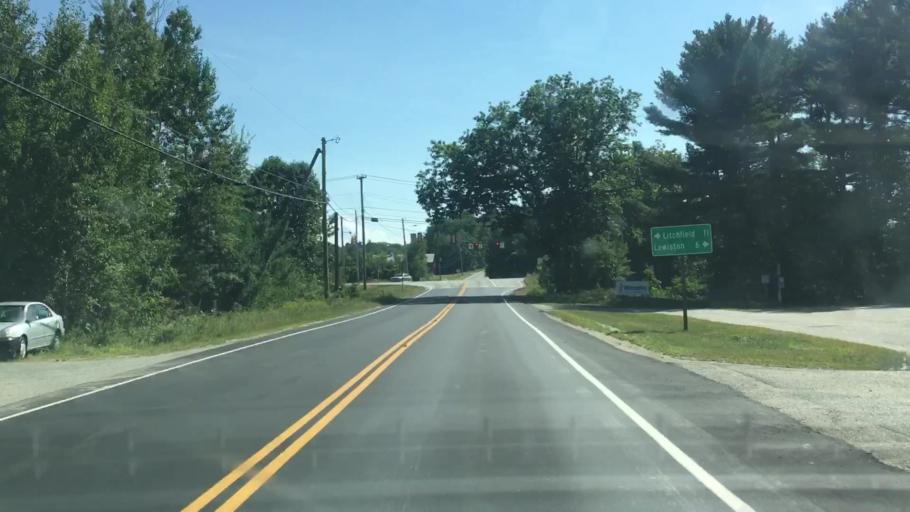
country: US
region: Maine
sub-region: Androscoggin County
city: Sabattus
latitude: 44.1221
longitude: -70.0858
